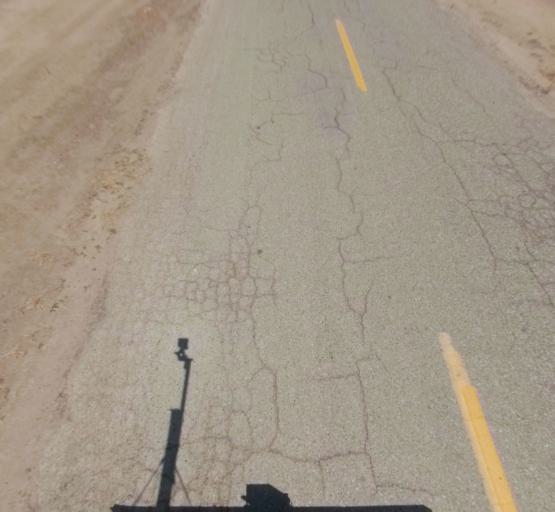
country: US
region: California
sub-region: Madera County
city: Chowchilla
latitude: 37.0882
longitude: -120.4370
